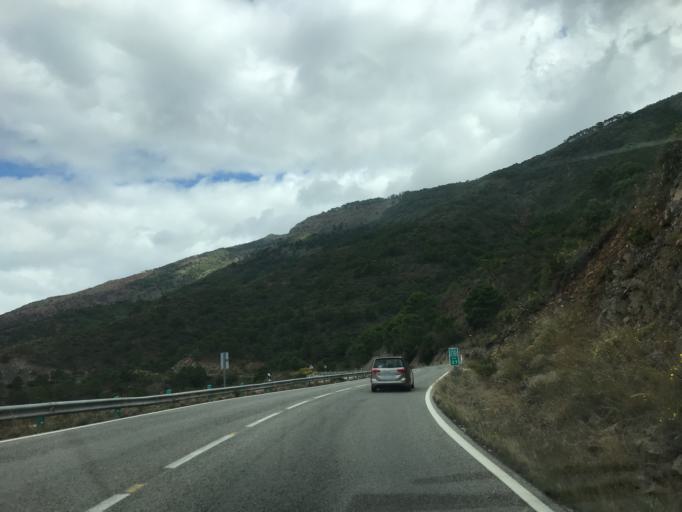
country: ES
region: Andalusia
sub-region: Provincia de Malaga
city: Benahavis
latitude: 36.5509
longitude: -5.0305
